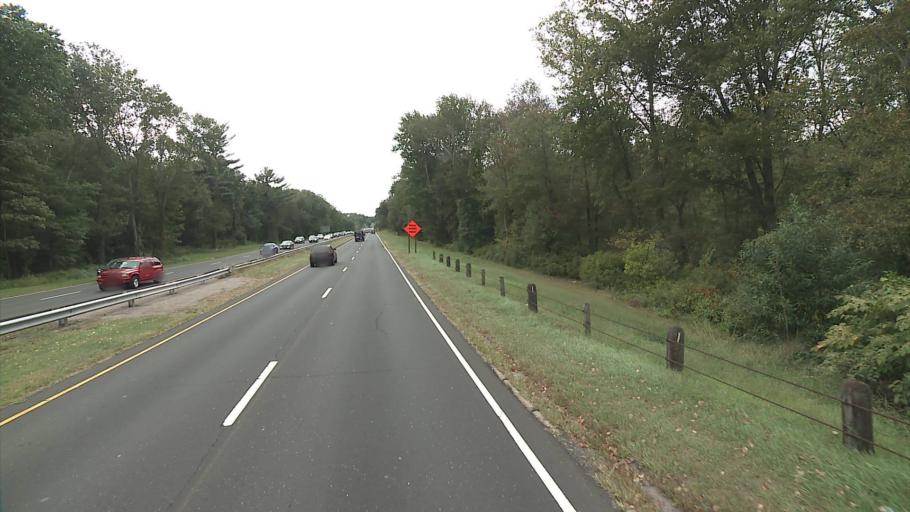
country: US
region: Connecticut
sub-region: Fairfield County
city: New Canaan
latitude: 41.1299
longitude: -73.4631
